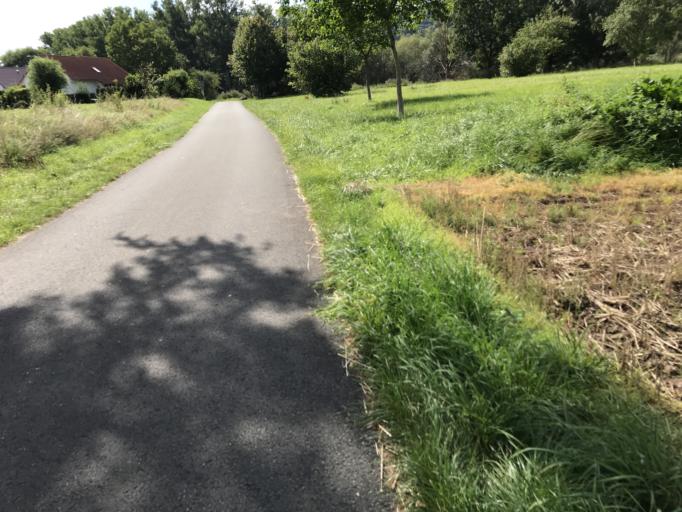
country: DE
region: Hesse
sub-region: Regierungsbezirk Kassel
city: Bad Sooden-Allendorf
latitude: 51.2776
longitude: 9.9671
